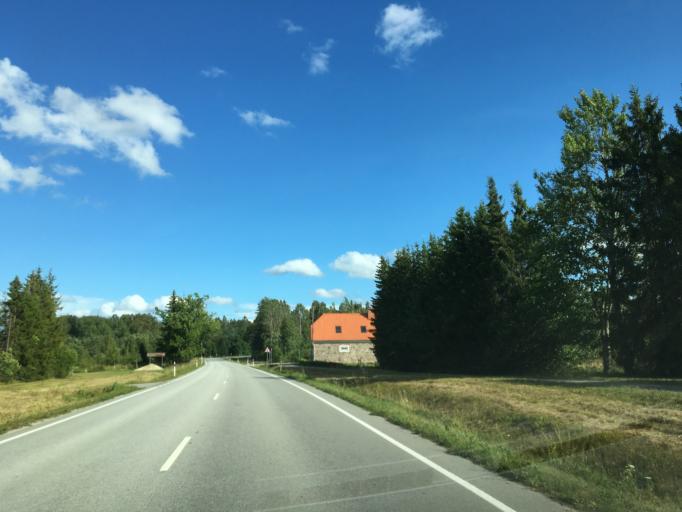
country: EE
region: Paernumaa
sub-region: Vaendra vald (alev)
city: Vandra
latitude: 58.6531
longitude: 25.0599
